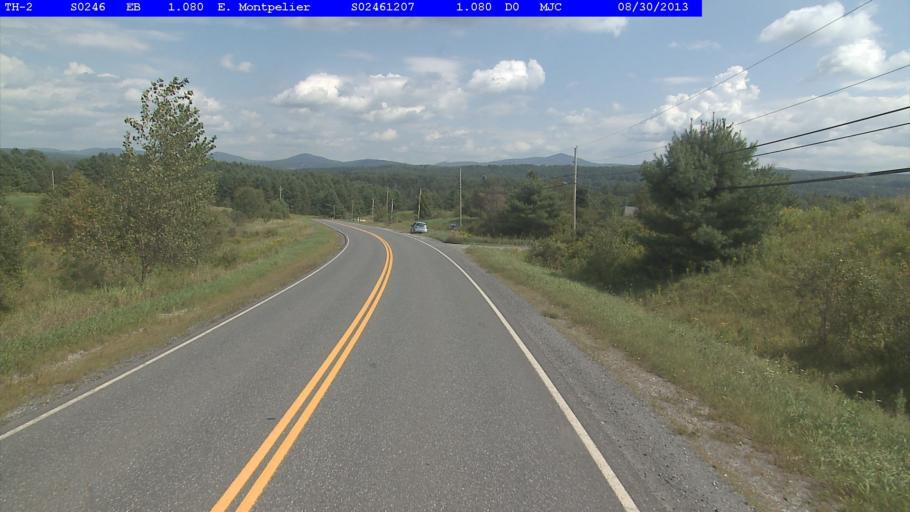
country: US
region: Vermont
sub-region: Washington County
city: Barre
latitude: 44.2619
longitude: -72.5058
